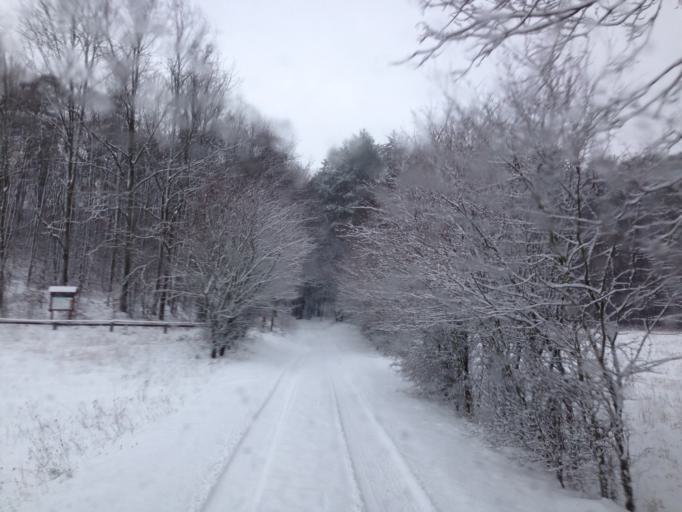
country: PL
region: Kujawsko-Pomorskie
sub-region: Powiat brodnicki
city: Gorzno
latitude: 53.1873
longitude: 19.6625
